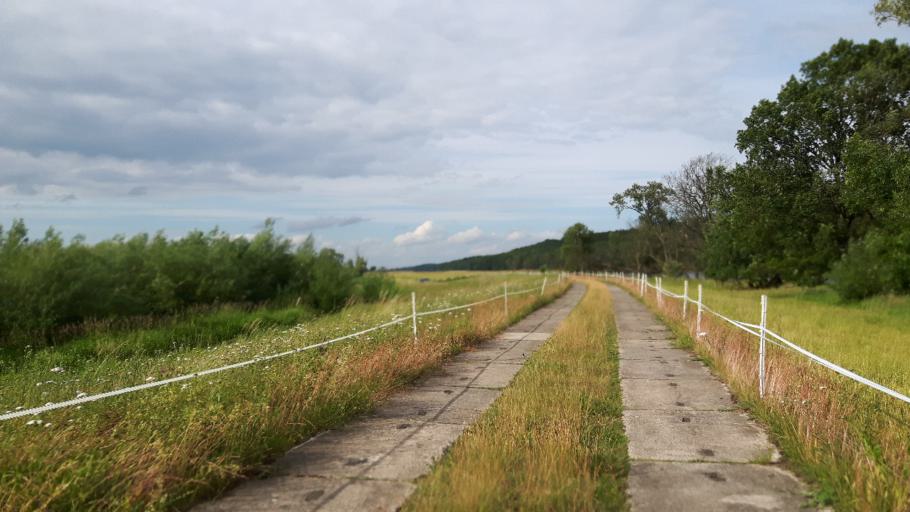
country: PL
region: West Pomeranian Voivodeship
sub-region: Powiat gryfinski
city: Widuchowa
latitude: 53.0870
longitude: 14.3659
